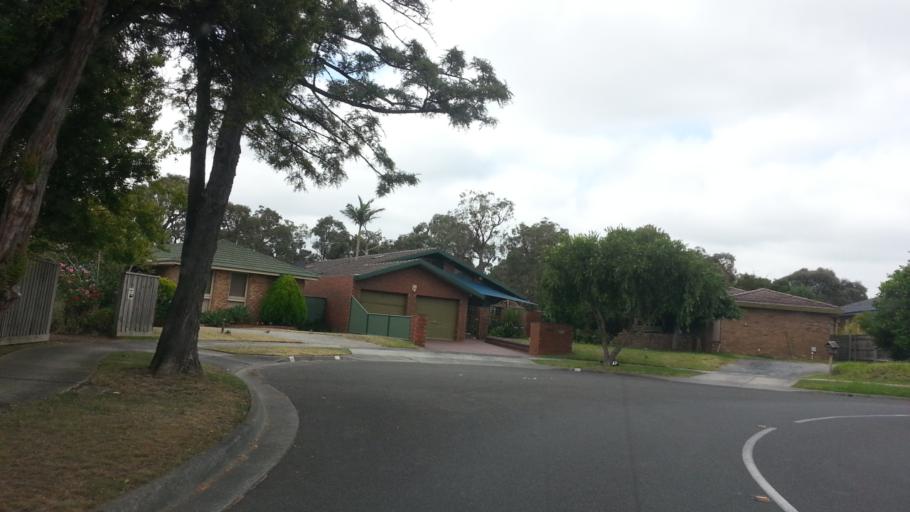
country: AU
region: Victoria
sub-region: Knox
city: Scoresby
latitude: -37.9104
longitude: 145.2506
